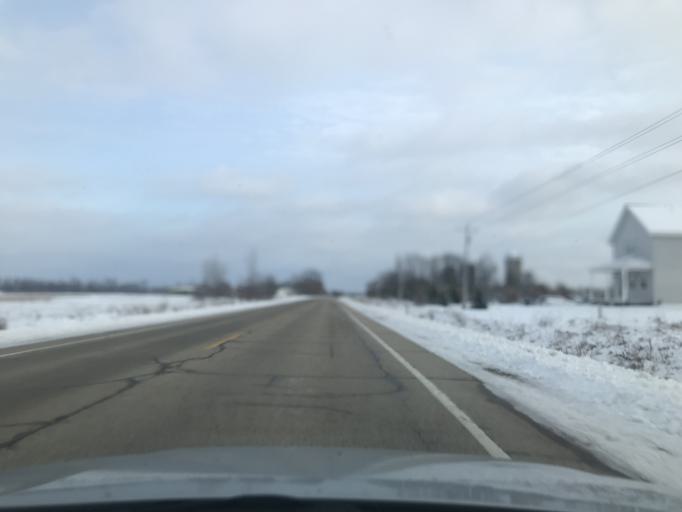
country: US
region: Wisconsin
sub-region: Oconto County
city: Oconto
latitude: 44.8927
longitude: -87.9409
